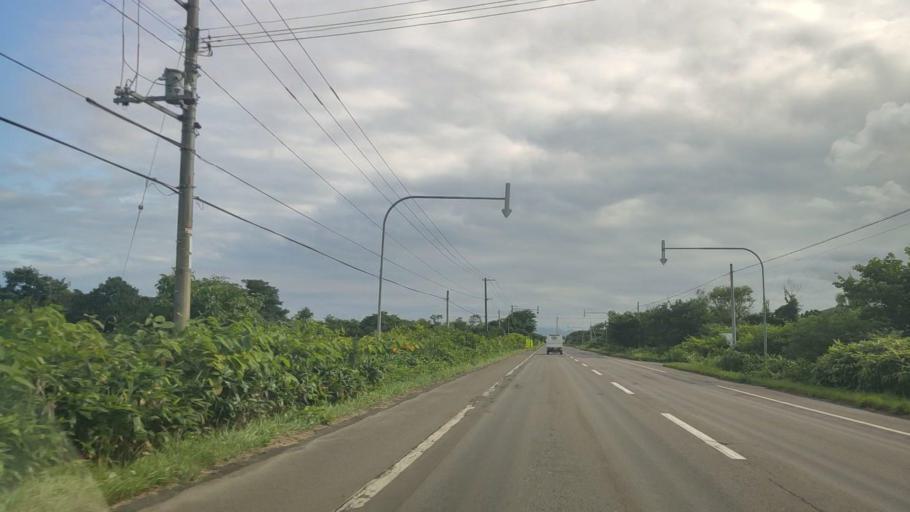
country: JP
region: Hokkaido
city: Niseko Town
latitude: 42.4648
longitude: 140.3392
